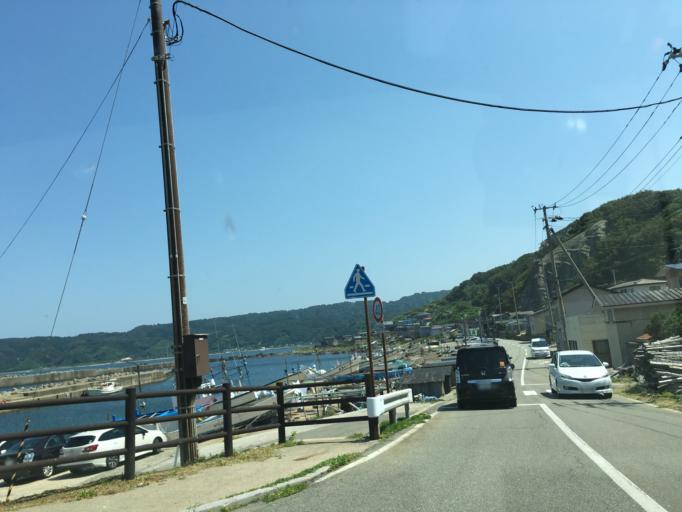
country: JP
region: Akita
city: Tenno
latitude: 39.9443
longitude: 139.7047
